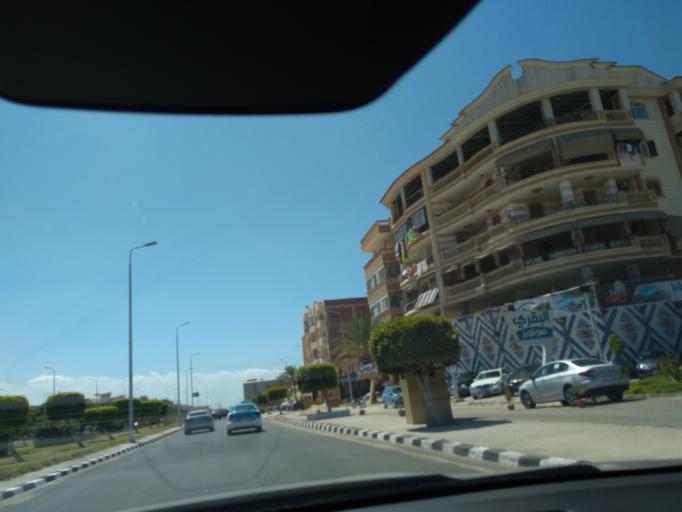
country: EG
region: Dumyat
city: Faraskur
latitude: 31.4354
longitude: 31.6744
